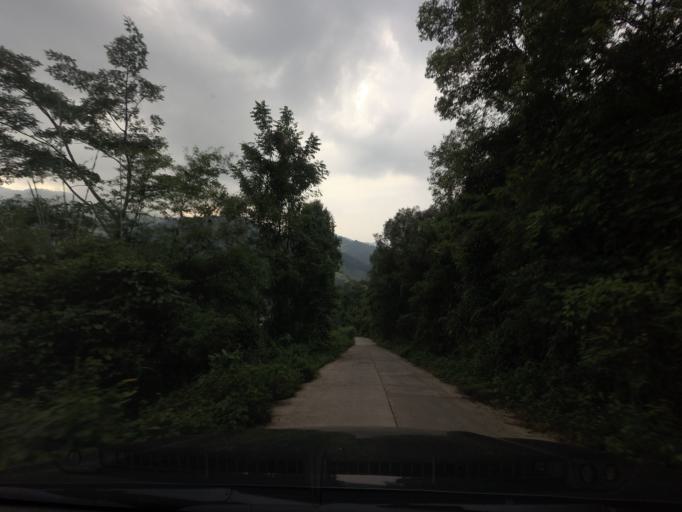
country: TH
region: Nan
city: Bo Kluea
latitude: 19.3497
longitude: 101.1639
